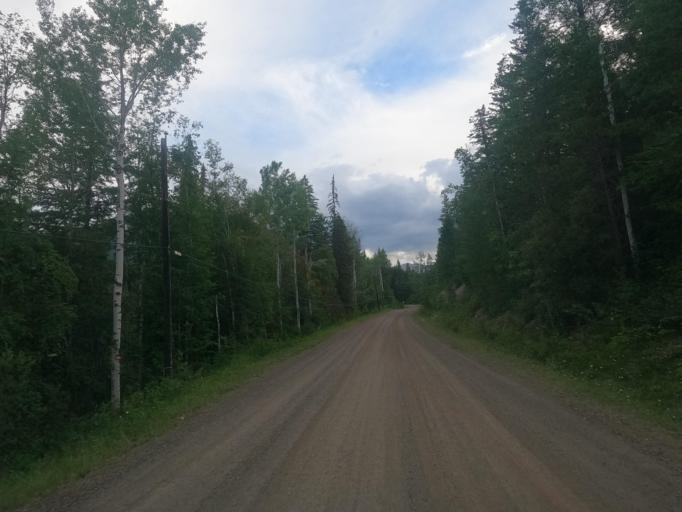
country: CA
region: British Columbia
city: Golden
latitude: 51.4519
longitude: -117.0037
